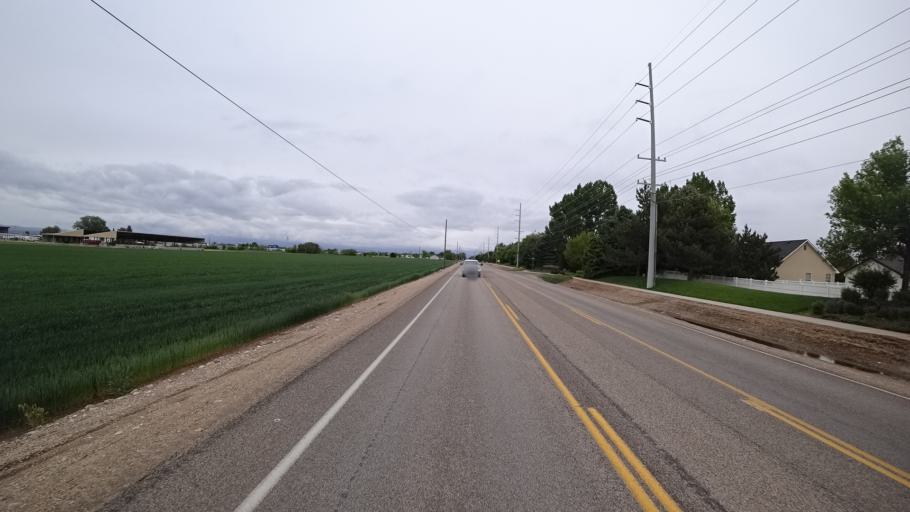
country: US
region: Idaho
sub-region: Ada County
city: Meridian
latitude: 43.6341
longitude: -116.4470
